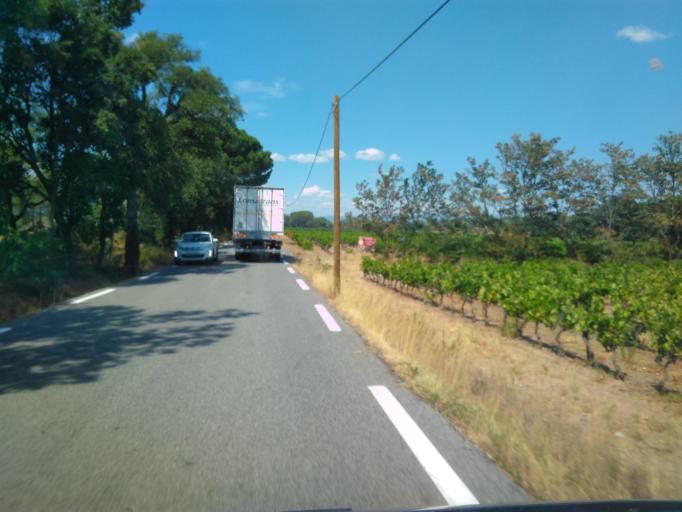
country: FR
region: Provence-Alpes-Cote d'Azur
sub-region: Departement du Var
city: La Garde-Freinet
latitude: 43.3460
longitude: 6.4278
